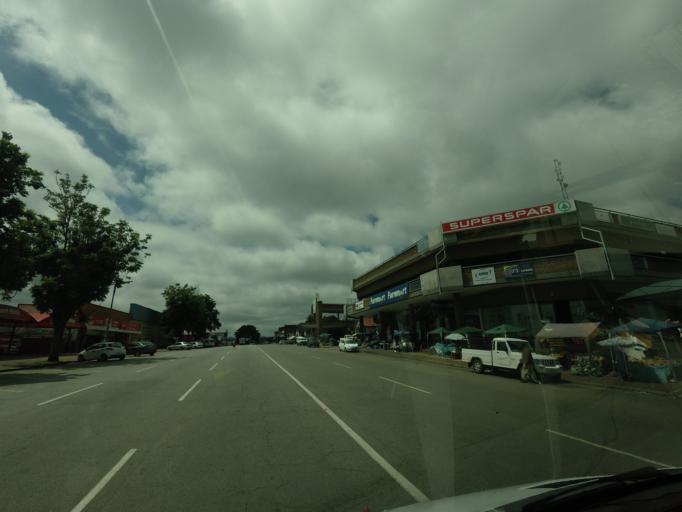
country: ZA
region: Mpumalanga
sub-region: Ehlanzeni District
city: White River
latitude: -25.3260
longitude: 31.0219
